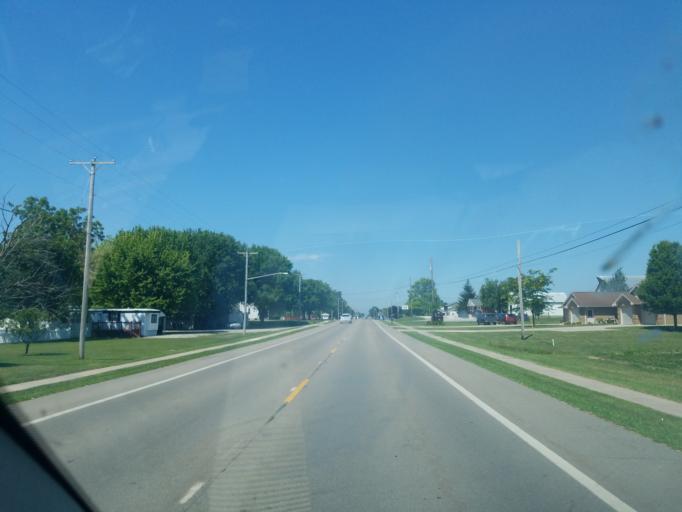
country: US
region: Ohio
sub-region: Auglaize County
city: New Bremen
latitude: 40.4077
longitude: -84.4857
